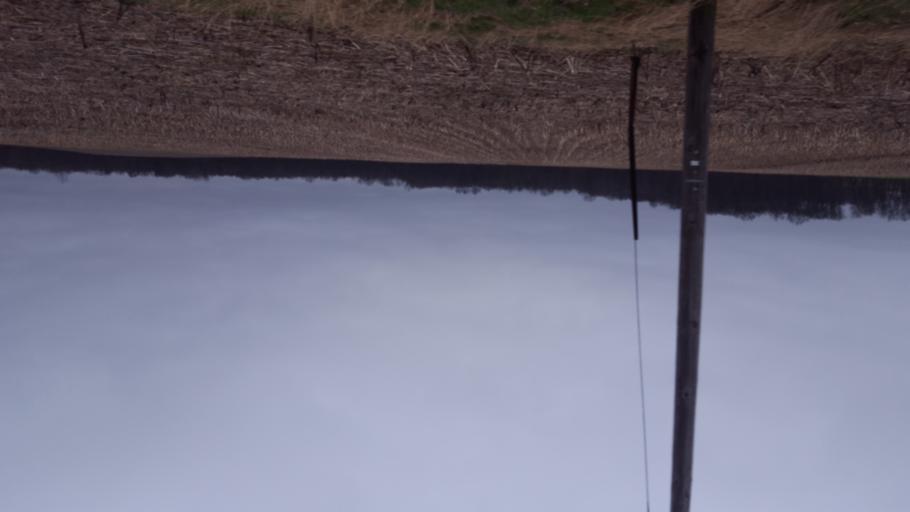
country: US
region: Ohio
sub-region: Knox County
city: Fredericktown
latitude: 40.5215
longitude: -82.5650
